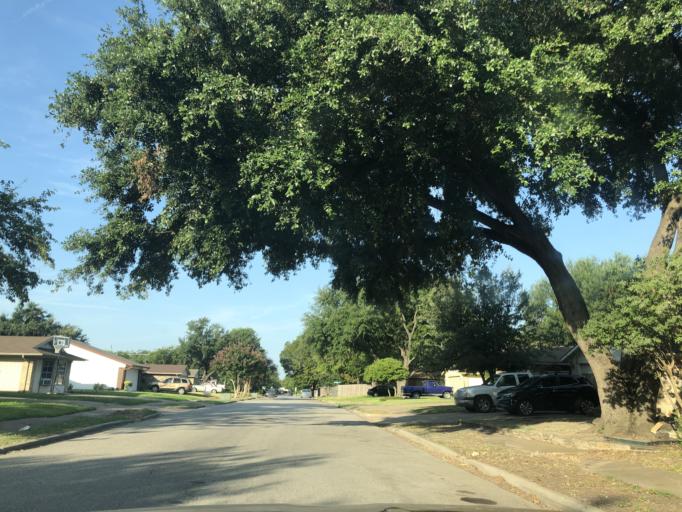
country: US
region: Texas
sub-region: Dallas County
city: Garland
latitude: 32.8509
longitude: -96.6316
